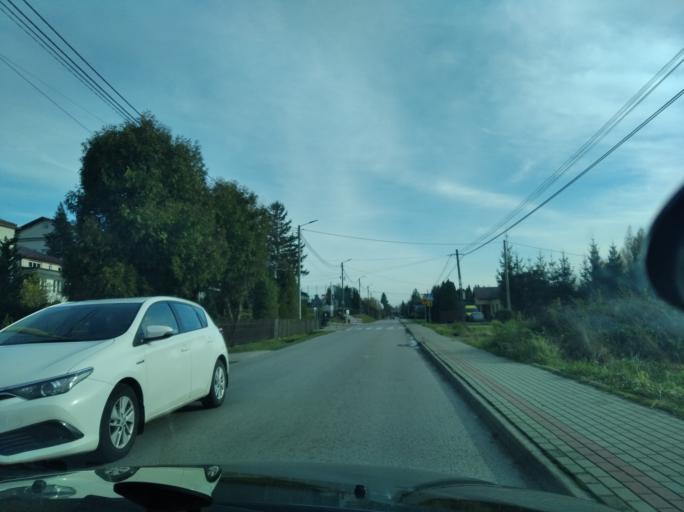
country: PL
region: Subcarpathian Voivodeship
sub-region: Powiat lancucki
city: Kraczkowa
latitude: 50.0381
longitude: 22.1601
